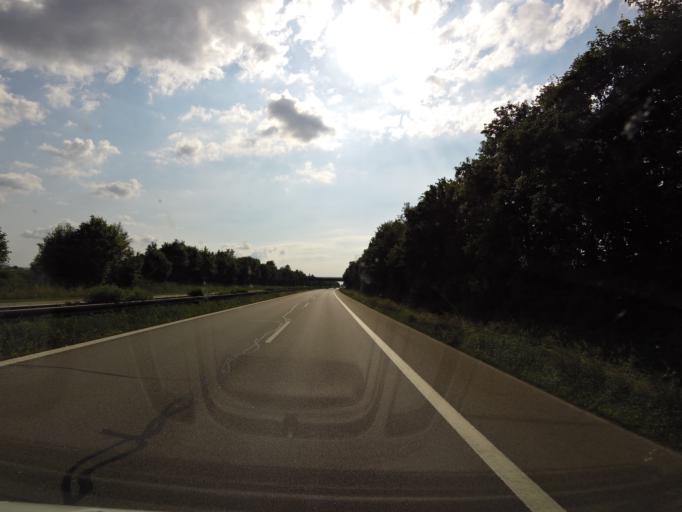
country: DE
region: Bavaria
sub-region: Lower Bavaria
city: Pilsting
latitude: 48.6856
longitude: 12.6361
